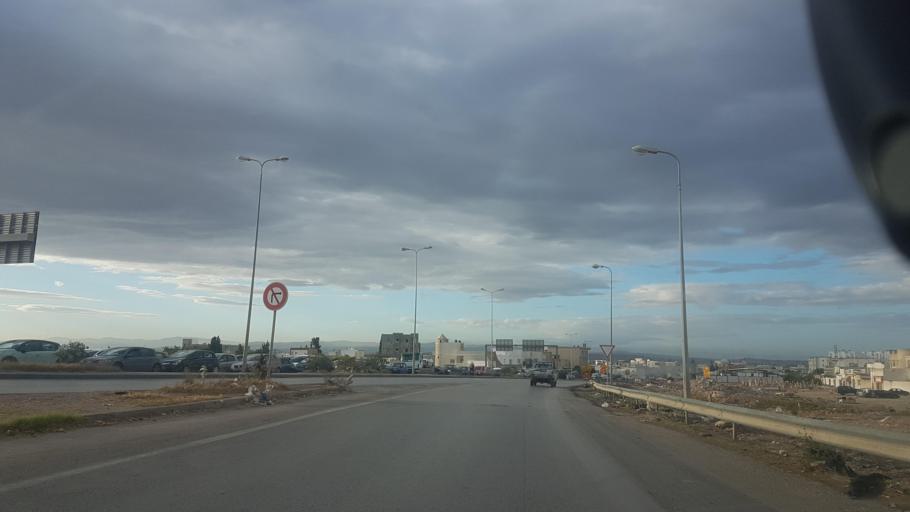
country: TN
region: Bin 'Arus
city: Ben Arous
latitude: 36.7448
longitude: 10.2082
